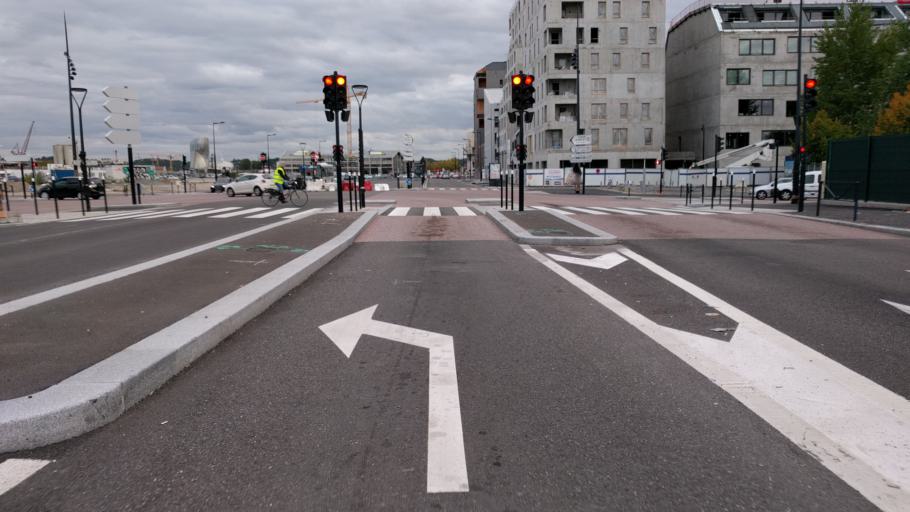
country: FR
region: Aquitaine
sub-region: Departement de la Gironde
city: Bordeaux
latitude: 44.8663
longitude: -0.5617
